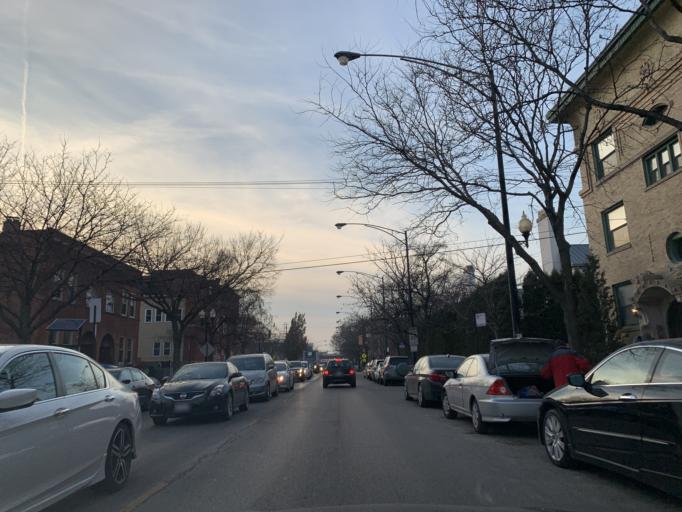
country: US
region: Illinois
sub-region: Cook County
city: Lincolnwood
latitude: 41.9616
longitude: -87.6713
